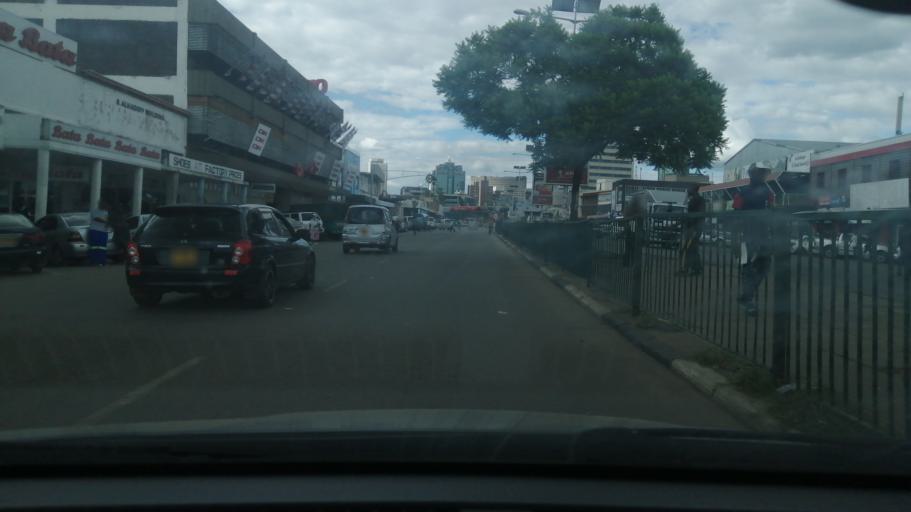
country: ZW
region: Harare
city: Harare
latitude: -17.8354
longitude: 31.0465
